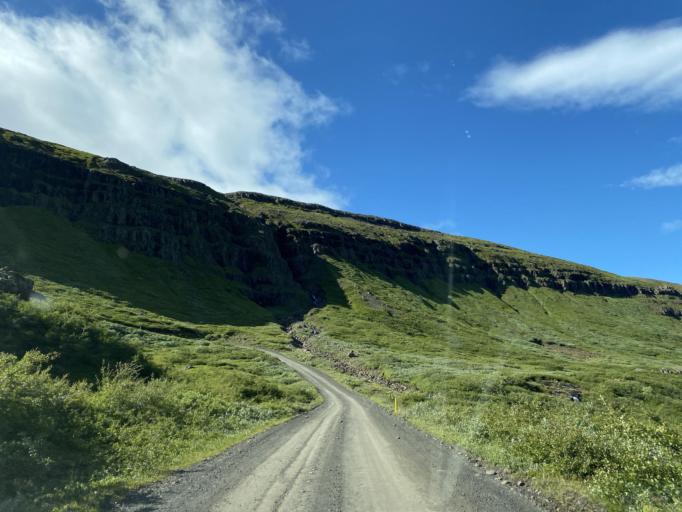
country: IS
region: East
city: Eskifjoerdur
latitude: 65.1822
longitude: -14.0801
